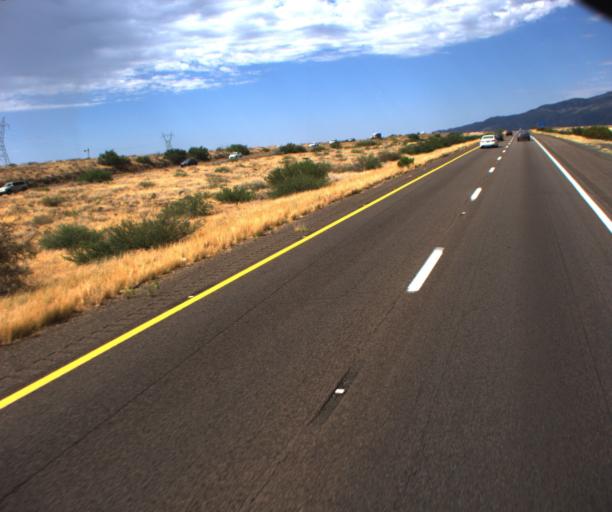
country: US
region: Arizona
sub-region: Yavapai County
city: Cordes Lakes
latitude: 34.2116
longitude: -112.1159
